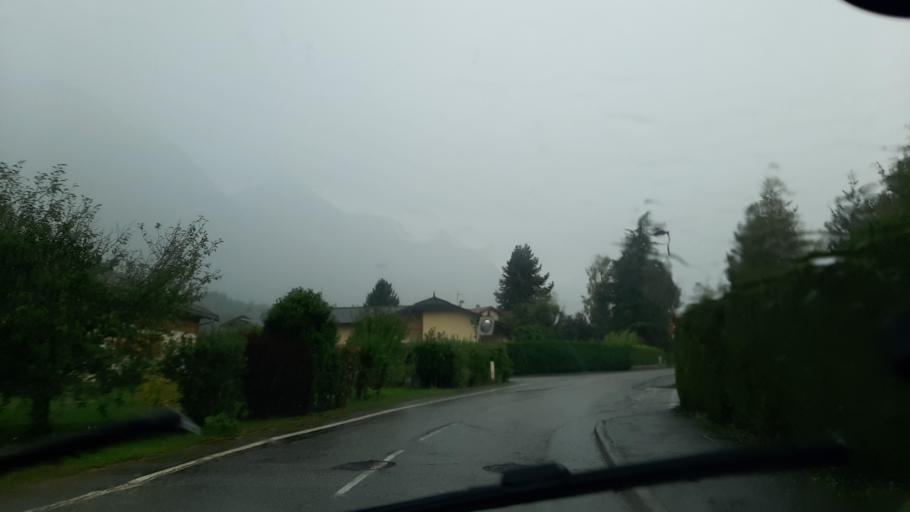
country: FR
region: Rhone-Alpes
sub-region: Departement de la Savoie
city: Gilly-sur-Isere
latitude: 45.6645
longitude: 6.3522
